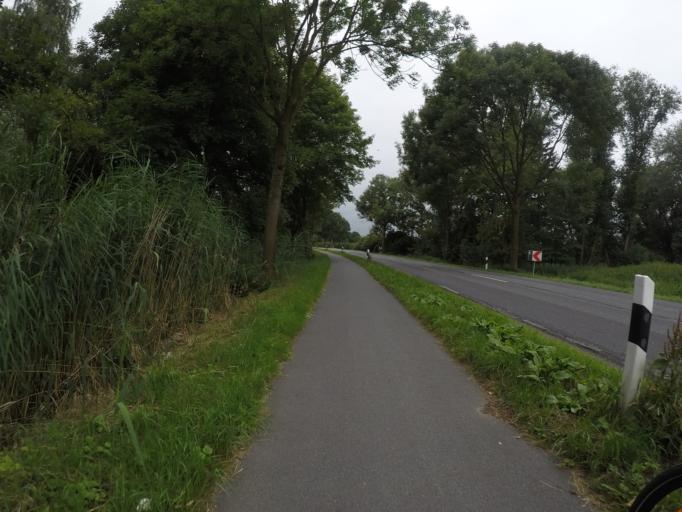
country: DE
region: Schleswig-Holstein
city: Wedel
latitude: 53.5431
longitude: 9.7372
